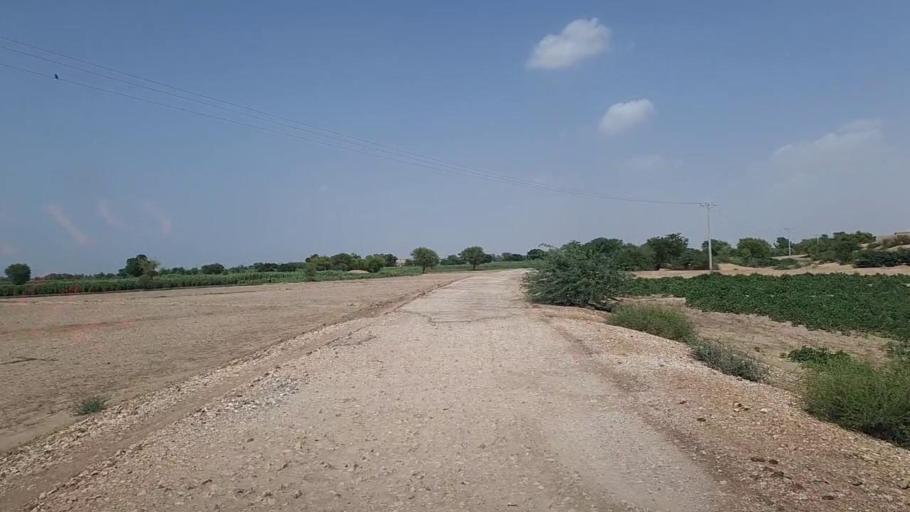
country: PK
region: Sindh
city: Pad Idan
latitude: 26.8010
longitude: 68.3690
